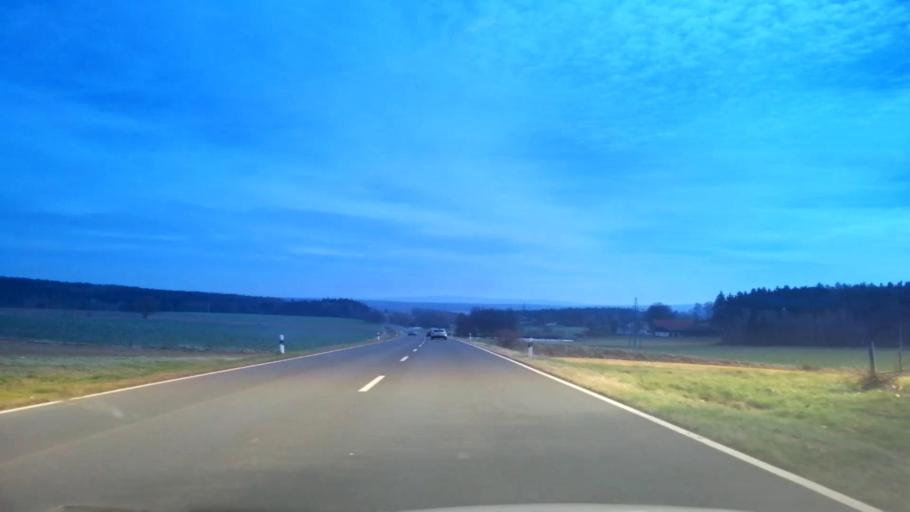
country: DE
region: Bavaria
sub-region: Upper Palatinate
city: Waldsassen
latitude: 50.0058
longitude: 12.2586
